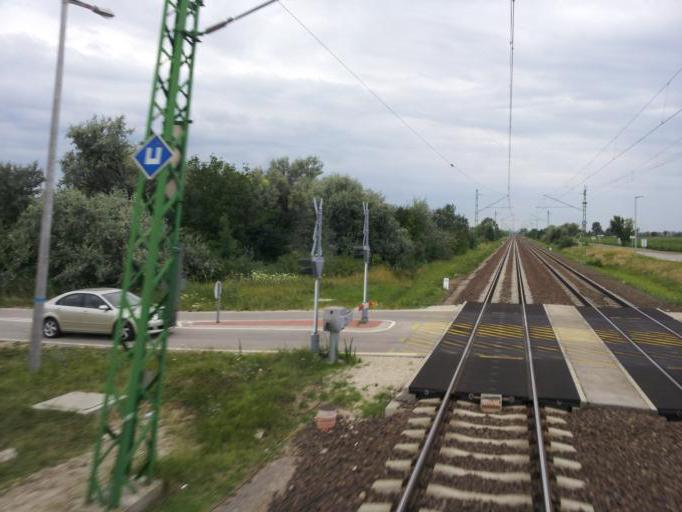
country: HU
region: Fejer
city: Pakozd
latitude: 47.1884
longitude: 18.5835
